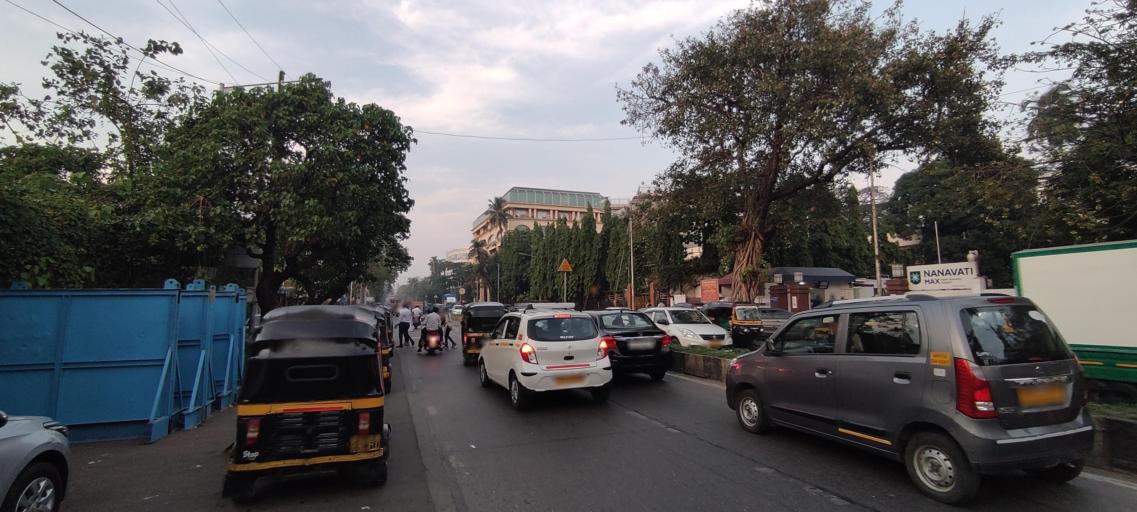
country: IN
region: Maharashtra
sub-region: Mumbai Suburban
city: Mumbai
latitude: 19.0960
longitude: 72.8395
